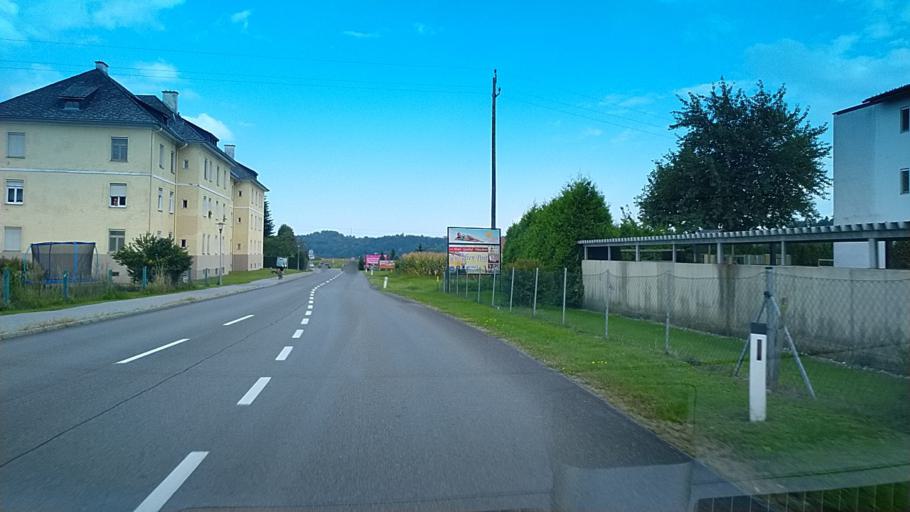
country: AT
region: Styria
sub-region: Politischer Bezirk Deutschlandsberg
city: Schwanberg
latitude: 46.7552
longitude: 15.2097
